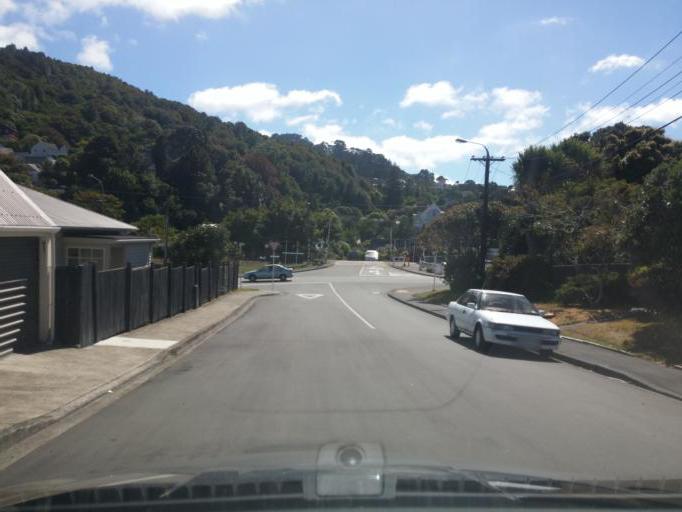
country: NZ
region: Wellington
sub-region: Wellington City
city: Kelburn
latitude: -41.2472
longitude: 174.7833
